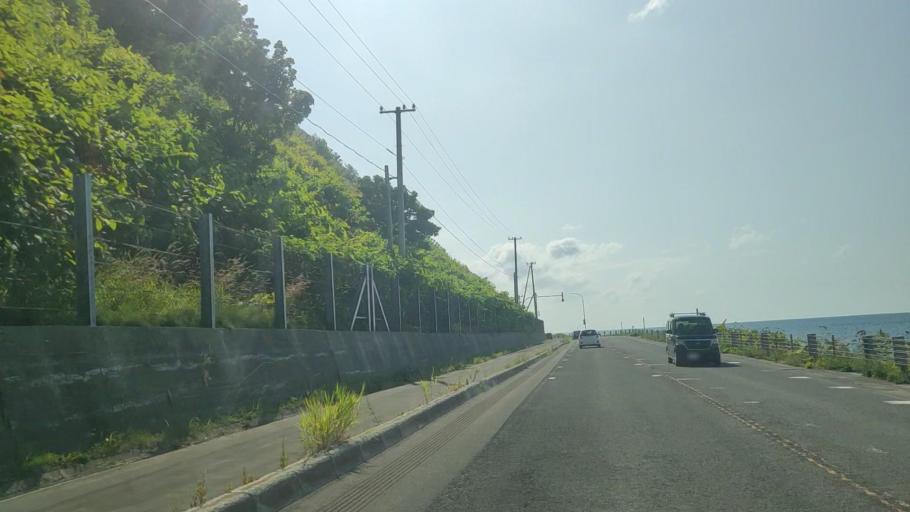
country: JP
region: Hokkaido
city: Rumoi
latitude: 43.8835
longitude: 141.5963
